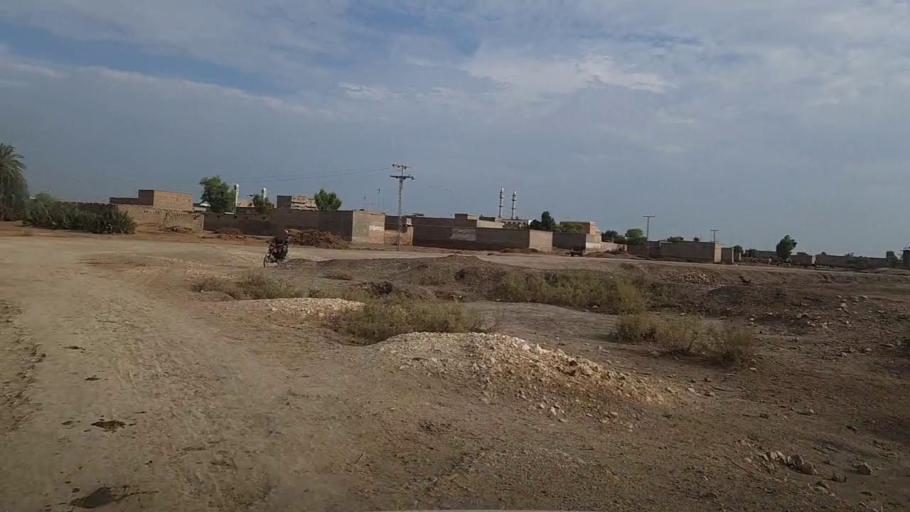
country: PK
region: Sindh
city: Thul
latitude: 28.2693
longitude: 68.8535
